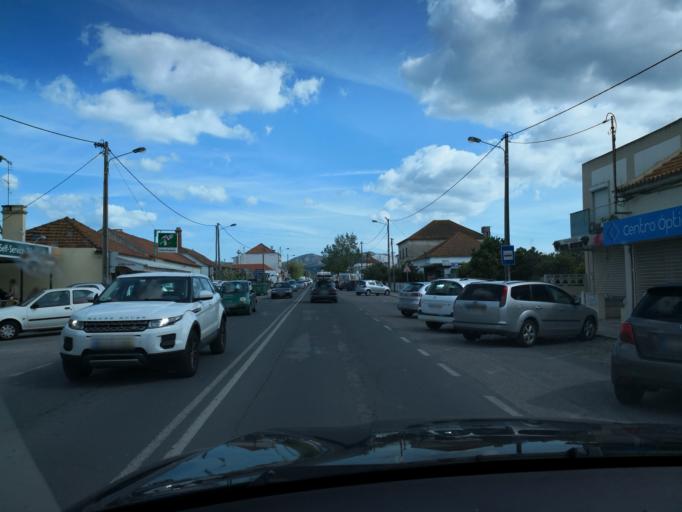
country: PT
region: Setubal
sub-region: Barreiro
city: Santo Antonio da Charneca
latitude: 38.5391
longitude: -9.0258
